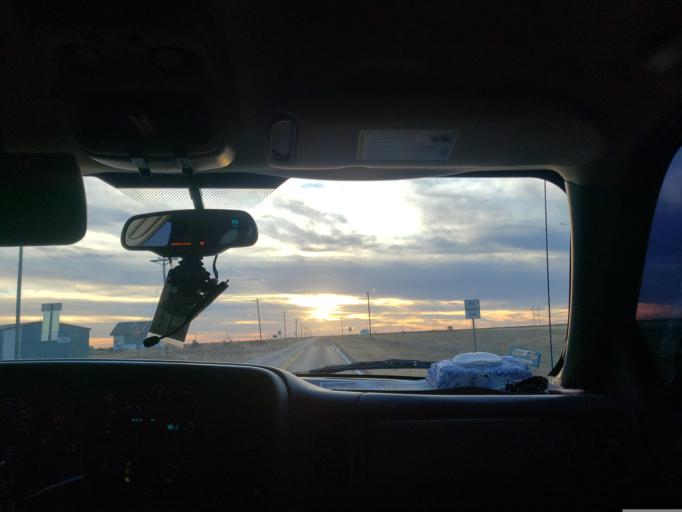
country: US
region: Oklahoma
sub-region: Cimarron County
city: Boise City
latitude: 36.8086
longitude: -102.2584
